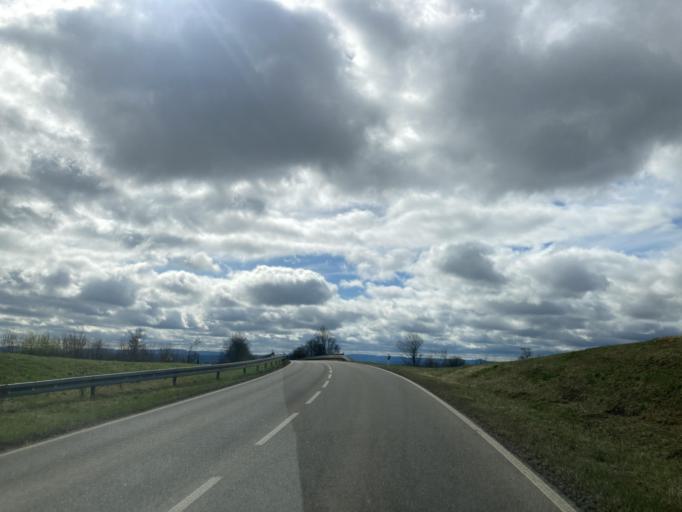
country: DE
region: Baden-Wuerttemberg
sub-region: Regierungsbezirk Stuttgart
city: Bondorf
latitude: 48.5168
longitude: 8.8691
